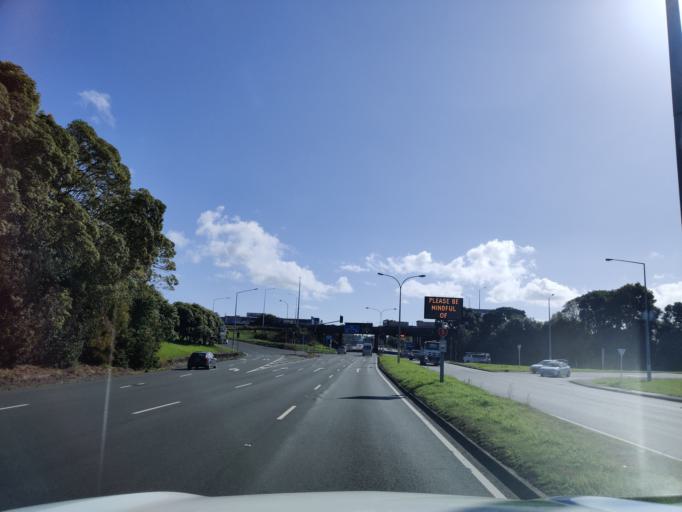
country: NZ
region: Auckland
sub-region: Auckland
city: Tamaki
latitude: -36.9203
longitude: 174.8403
